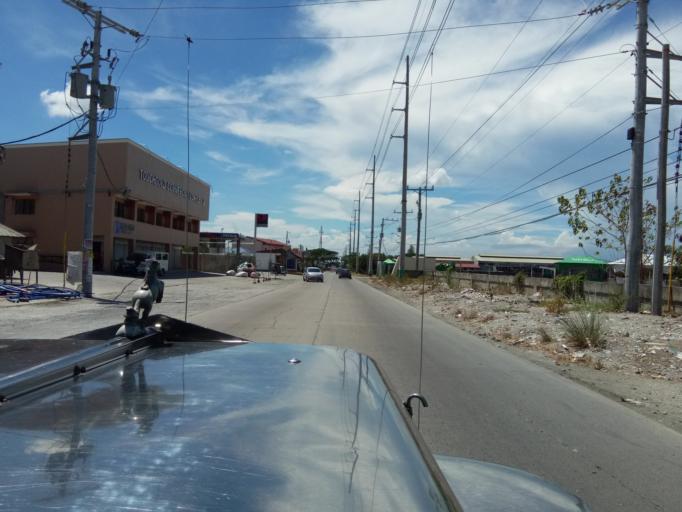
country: PH
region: Calabarzon
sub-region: Province of Cavite
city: Pasong Kawayan Primero
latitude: 14.3523
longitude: 120.9014
